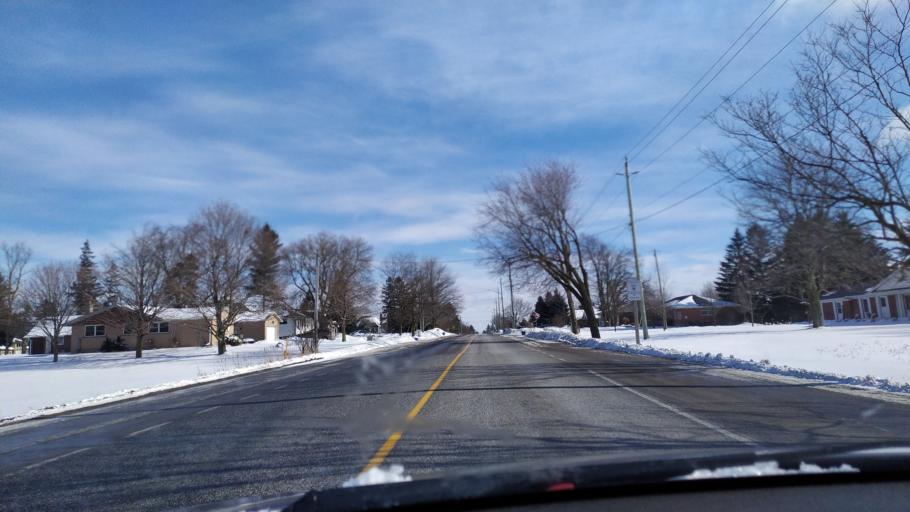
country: CA
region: Ontario
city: Waterloo
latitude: 43.5238
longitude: -80.6611
